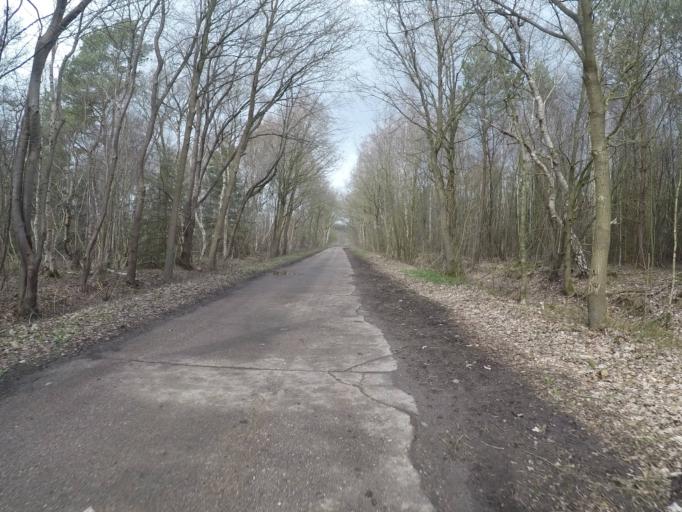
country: DE
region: Lower Saxony
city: Elmlohe
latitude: 53.6057
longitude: 8.7233
